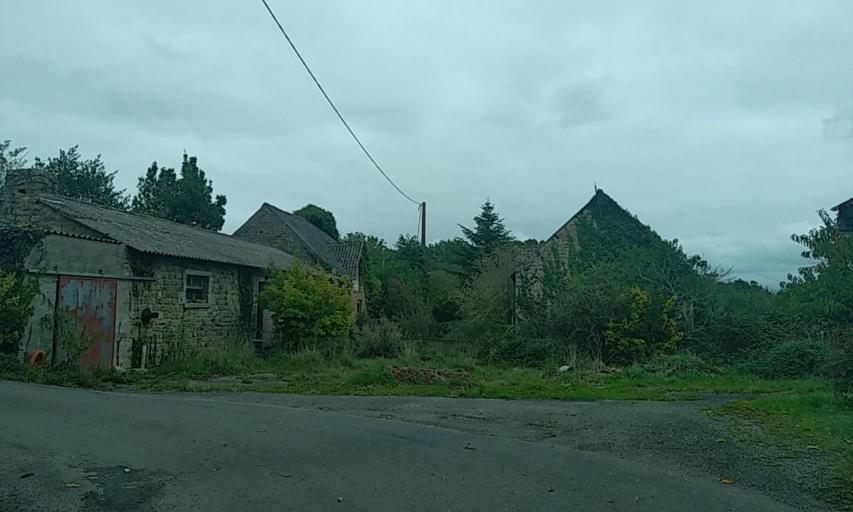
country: FR
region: Brittany
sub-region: Departement du Morbihan
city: Pont-Scorff
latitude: 47.8062
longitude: -3.3840
